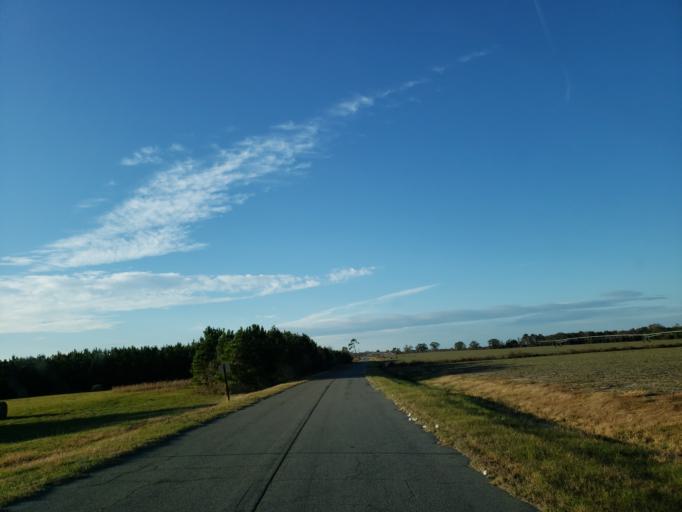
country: US
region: Georgia
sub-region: Dooly County
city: Unadilla
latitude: 32.1996
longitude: -83.7657
